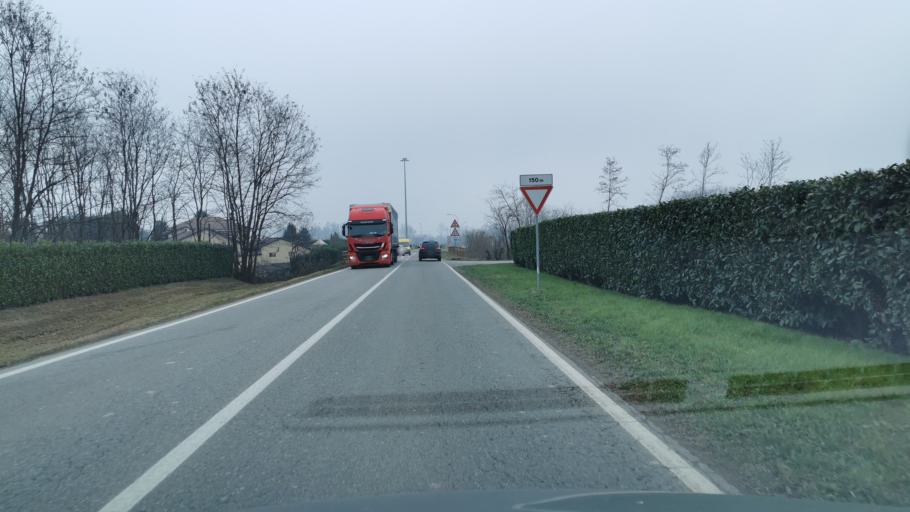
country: IT
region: Piedmont
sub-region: Provincia di Torino
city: Busano
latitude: 45.3247
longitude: 7.6563
